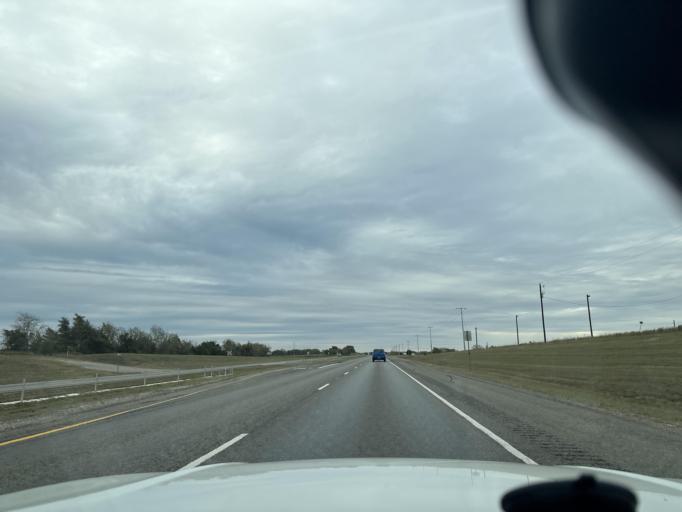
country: US
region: Texas
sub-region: Burleson County
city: Somerville
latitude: 30.1602
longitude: -96.6196
